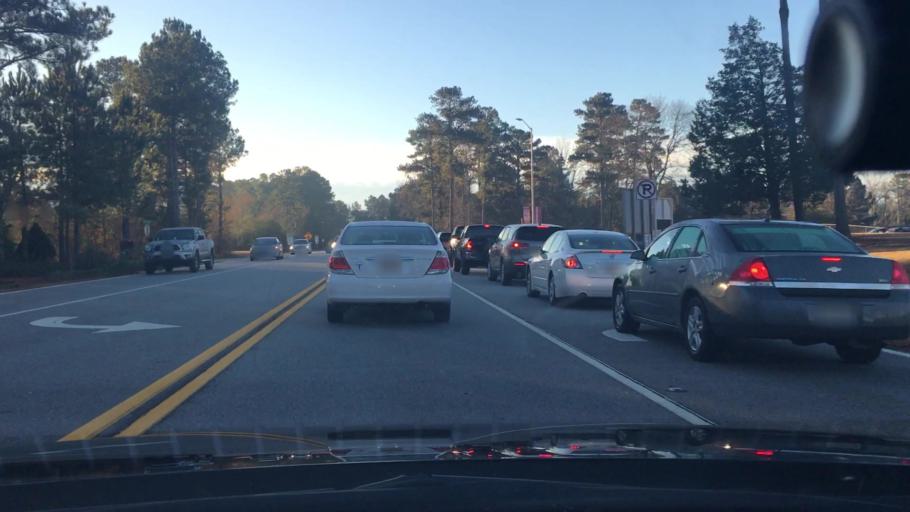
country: US
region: Georgia
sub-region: Fayette County
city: Peachtree City
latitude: 33.3477
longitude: -84.6563
